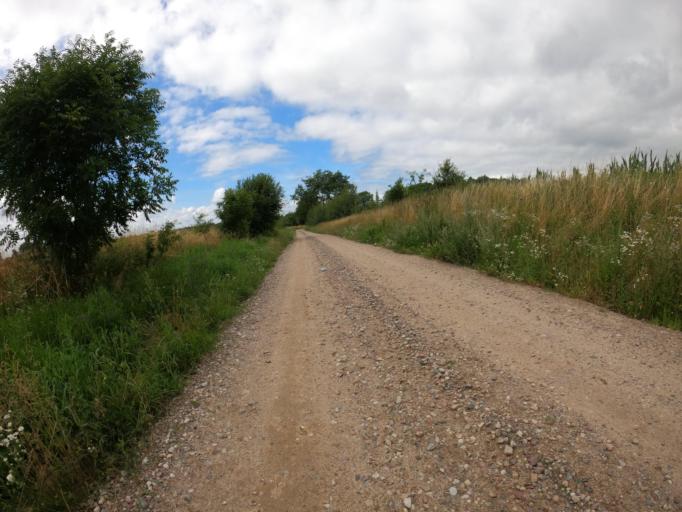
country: PL
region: West Pomeranian Voivodeship
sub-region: Powiat bialogardzki
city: Tychowo
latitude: 53.9993
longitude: 16.3746
